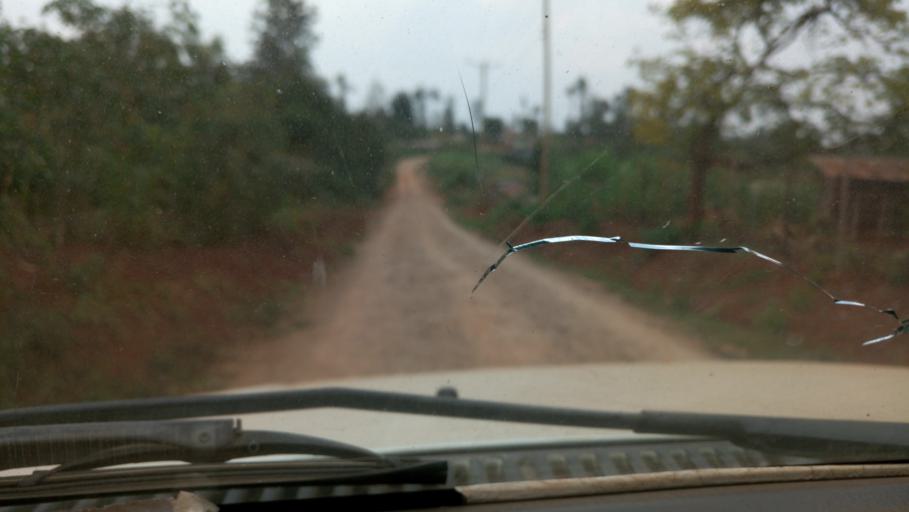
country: KE
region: Murang'a District
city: Kangema
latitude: -0.8109
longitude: 36.9918
